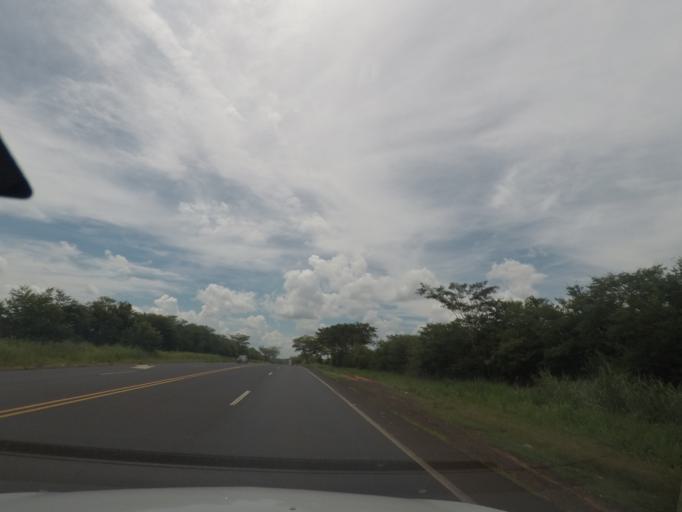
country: BR
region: Sao Paulo
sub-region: Barretos
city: Barretos
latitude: -20.4196
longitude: -48.6310
